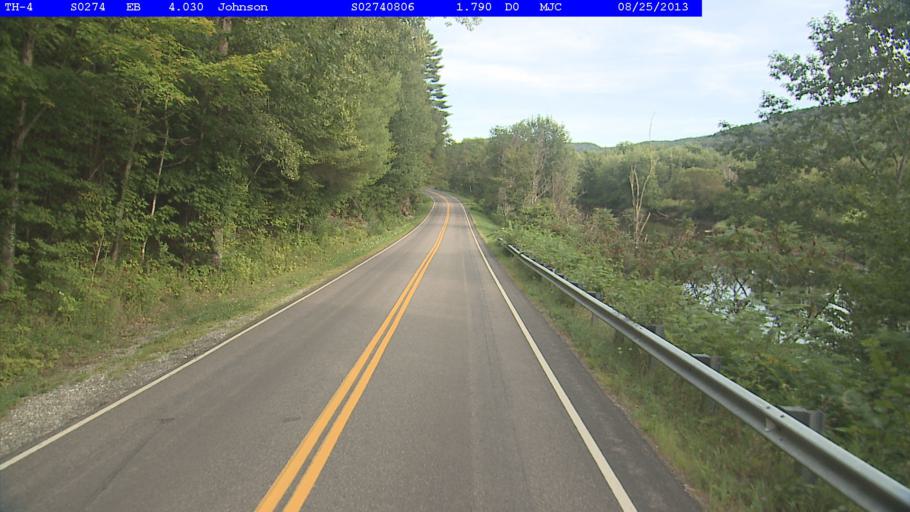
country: US
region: Vermont
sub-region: Lamoille County
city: Johnson
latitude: 44.6462
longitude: -72.7206
